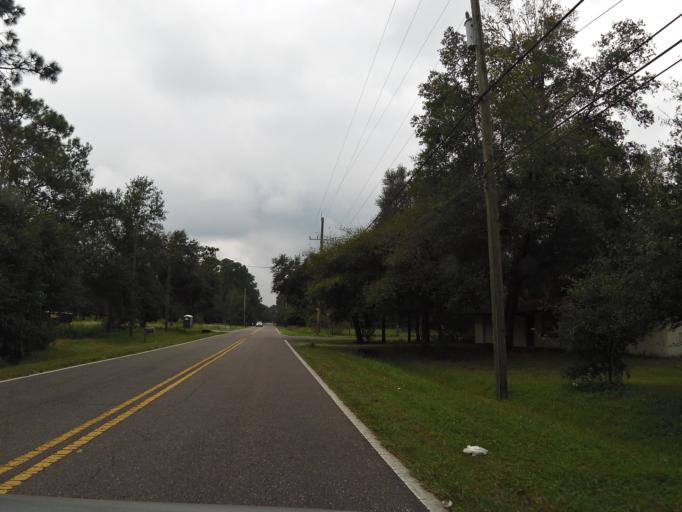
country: US
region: Florida
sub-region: Clay County
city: Bellair-Meadowbrook Terrace
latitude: 30.2179
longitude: -81.7727
